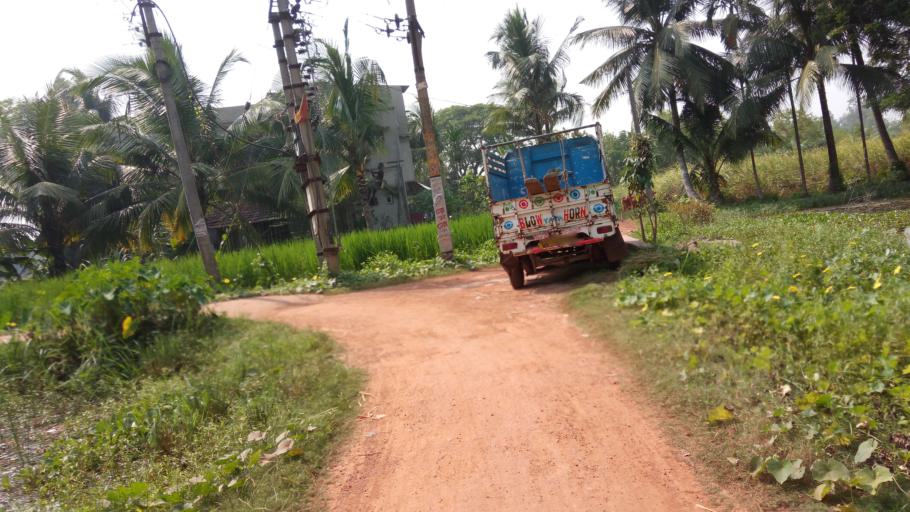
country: IN
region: West Bengal
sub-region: Purba Medinipur
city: Mahishadal
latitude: 22.1713
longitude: 87.9116
